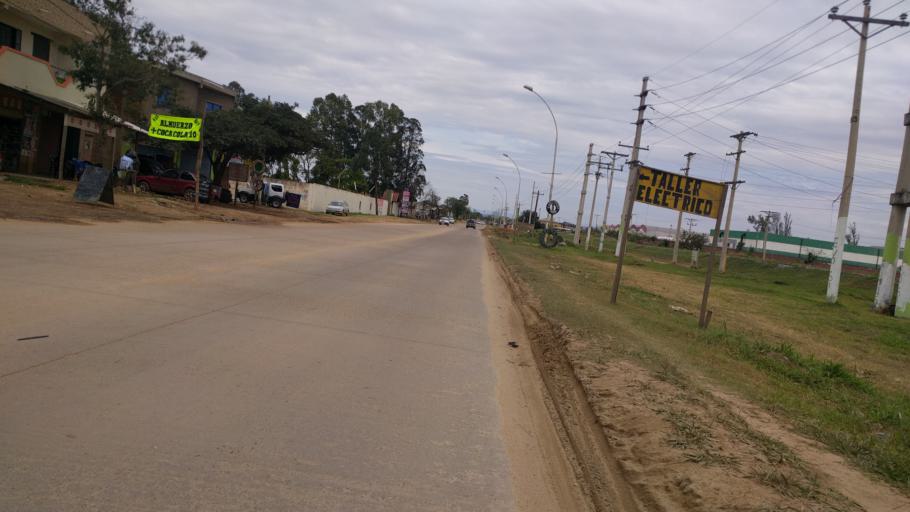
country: BO
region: Santa Cruz
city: Santa Cruz de la Sierra
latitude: -17.8483
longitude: -63.1777
